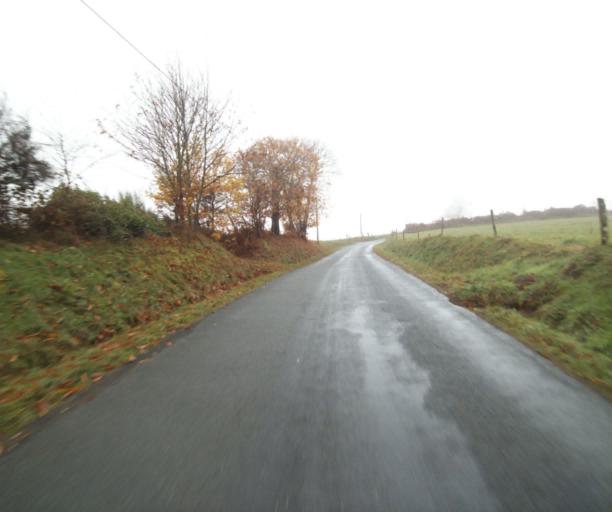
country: FR
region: Limousin
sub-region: Departement de la Correze
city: Cornil
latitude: 45.2001
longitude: 1.6372
